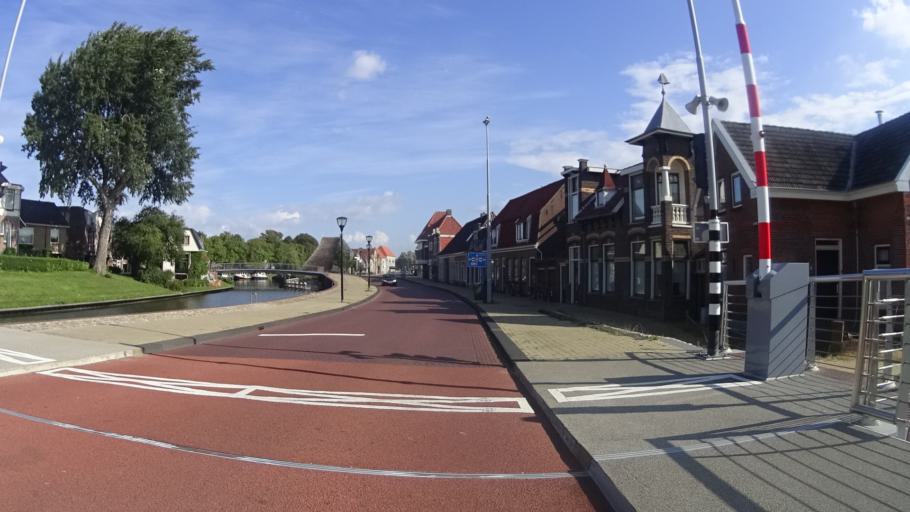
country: NL
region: Friesland
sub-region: Gemeente Franekeradeel
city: Franeker
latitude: 53.1844
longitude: 5.5487
